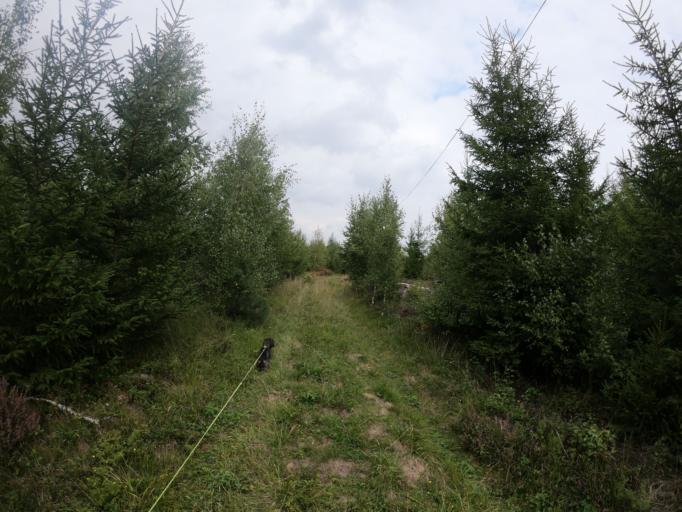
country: SE
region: Joenkoeping
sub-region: Vetlanda Kommun
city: Landsbro
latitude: 57.3151
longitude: 14.8588
